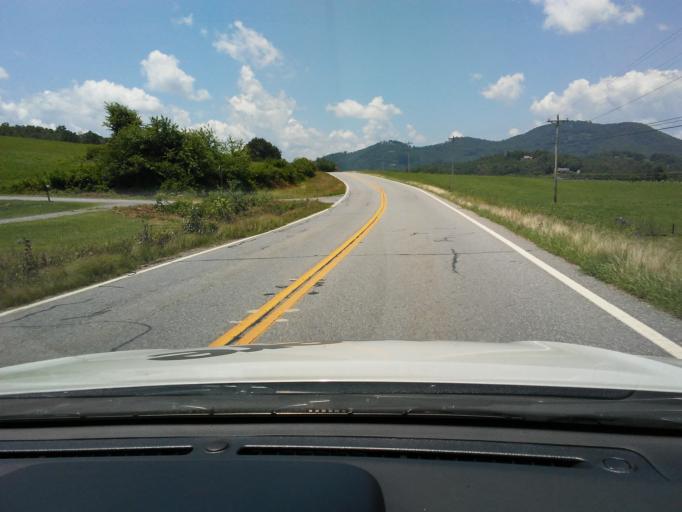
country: US
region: Georgia
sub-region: Towns County
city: Hiawassee
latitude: 34.9145
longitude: -83.7272
